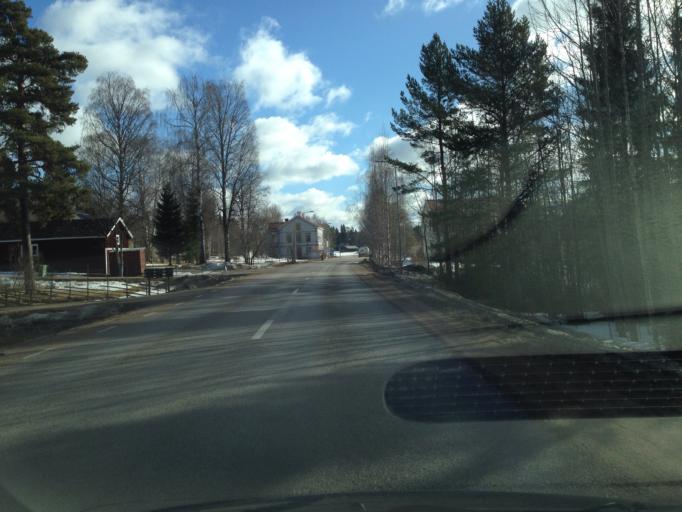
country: SE
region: Gaevleborg
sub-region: Ljusdals Kommun
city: Farila
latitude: 61.9873
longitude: 15.2944
